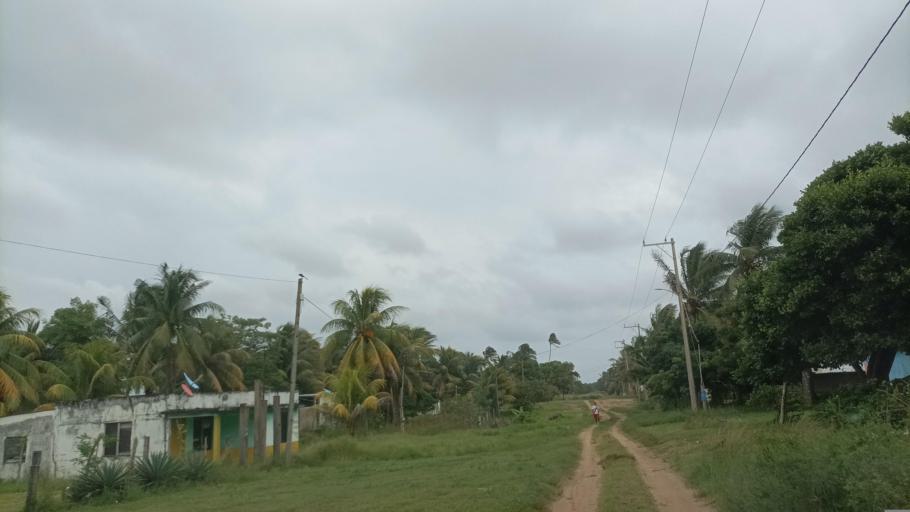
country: MX
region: Veracruz
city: Agua Dulce
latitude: 18.2073
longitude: -94.1456
